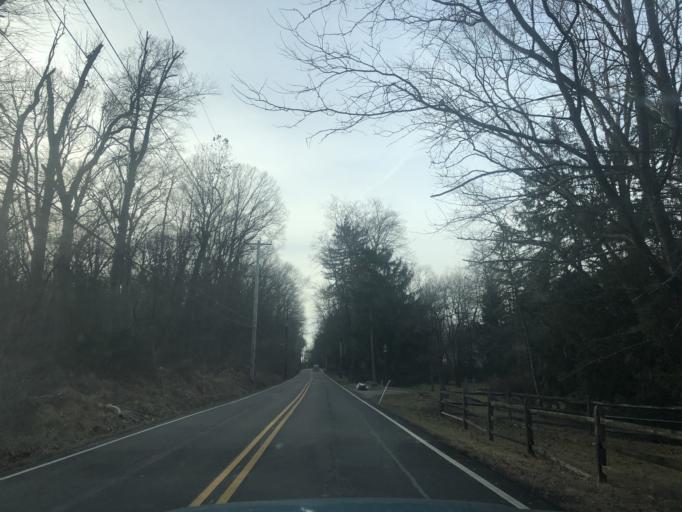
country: US
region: Pennsylvania
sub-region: Montgomery County
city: Flourtown
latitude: 40.1219
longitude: -75.2344
